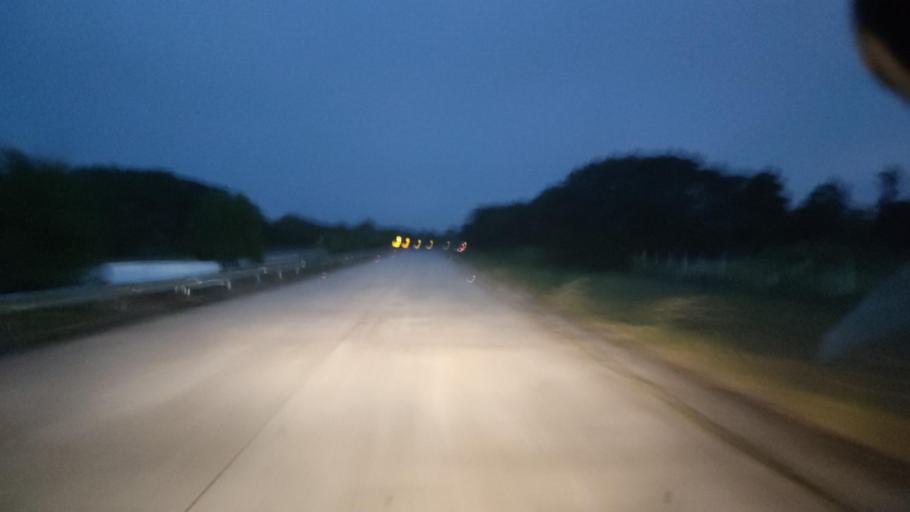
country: MM
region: Mandalay
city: Nay Pyi Taw
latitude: 19.9835
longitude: 95.9832
